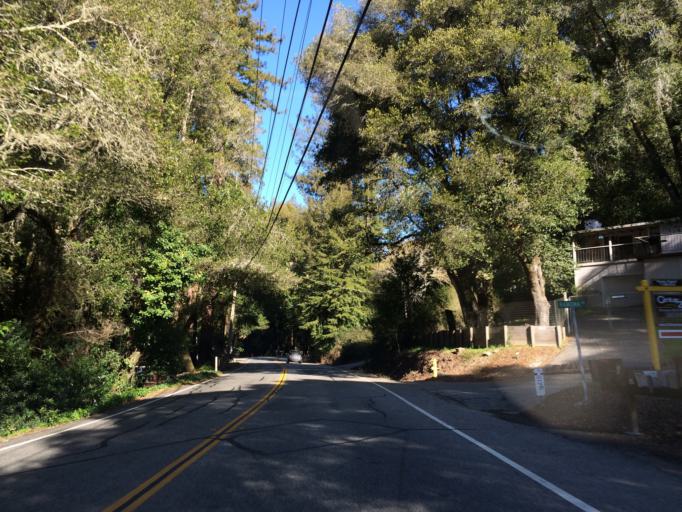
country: US
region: California
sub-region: Santa Cruz County
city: Boulder Creek
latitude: 37.1851
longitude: -122.1414
